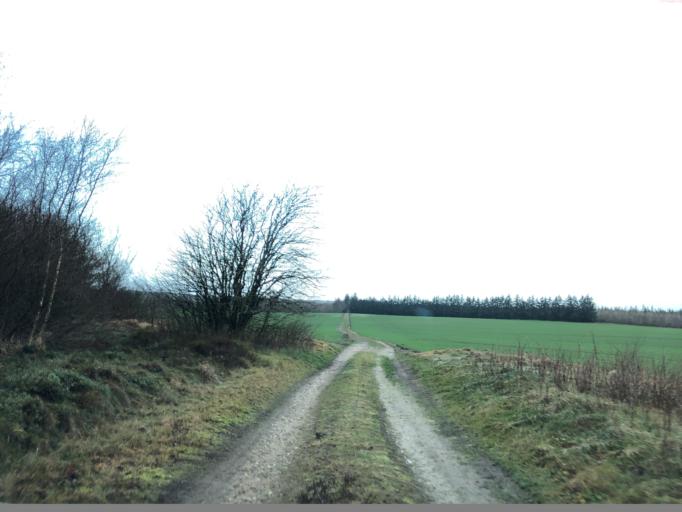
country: DK
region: Central Jutland
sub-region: Ringkobing-Skjern Kommune
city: Videbaek
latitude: 56.1867
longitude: 8.6602
